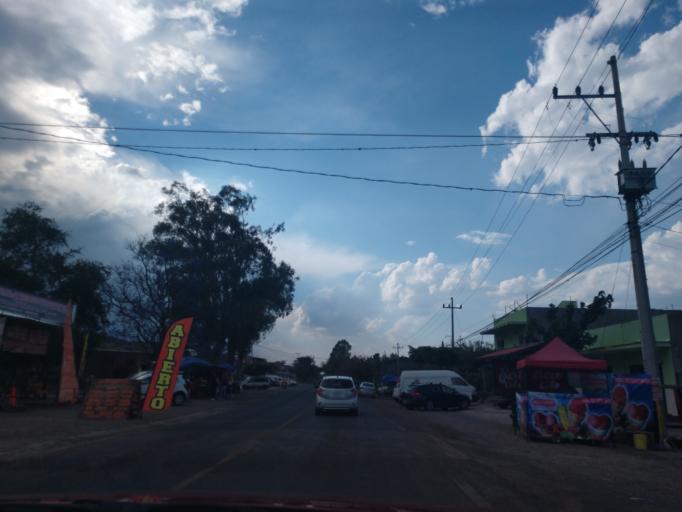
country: MX
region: Jalisco
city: San Juan Cosala
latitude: 20.2014
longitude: -103.3108
